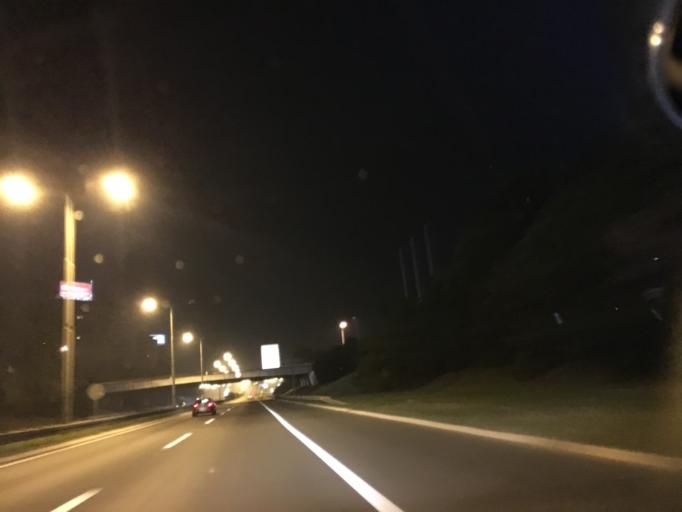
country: RS
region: Central Serbia
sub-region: Belgrade
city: Novi Beograd
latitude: 44.8195
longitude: 20.4050
